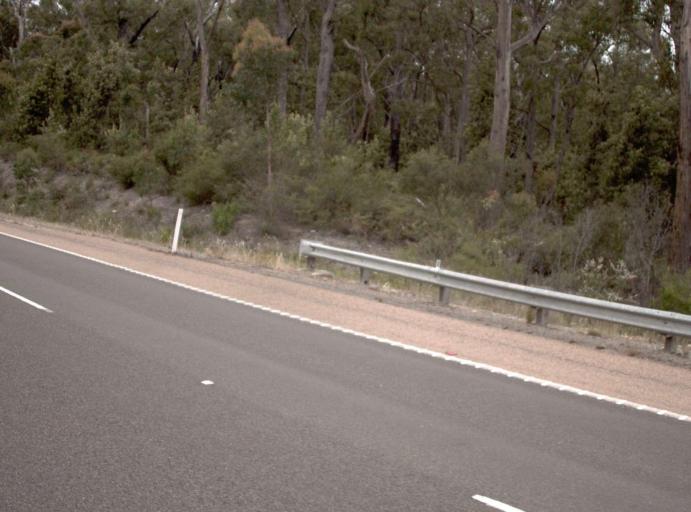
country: AU
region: Victoria
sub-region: East Gippsland
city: Lakes Entrance
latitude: -37.6971
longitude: 147.9952
